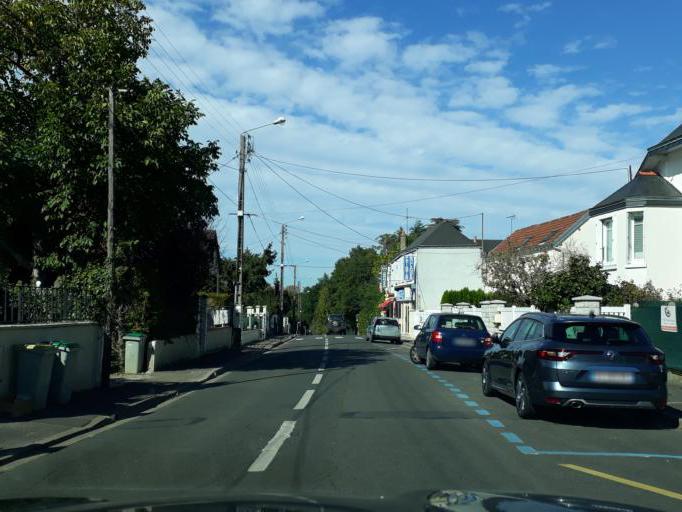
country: FR
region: Centre
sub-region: Departement d'Indre-et-Loire
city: Saint-Avertin
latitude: 47.3579
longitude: 0.7314
